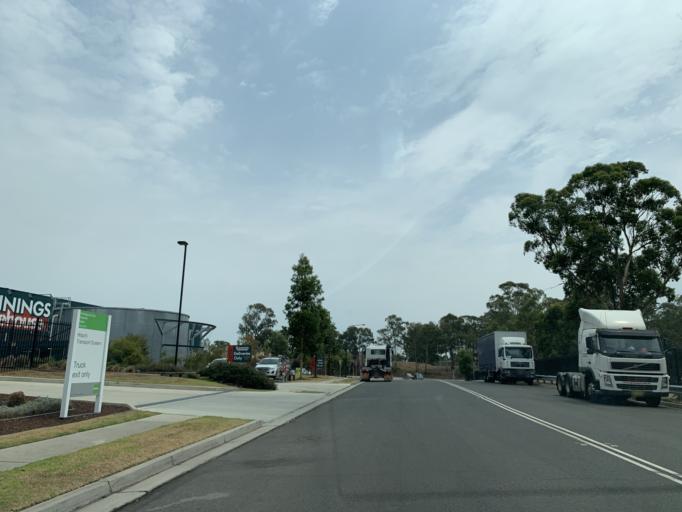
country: AU
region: New South Wales
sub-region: Blacktown
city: Blacktown
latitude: -33.8005
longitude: 150.8998
